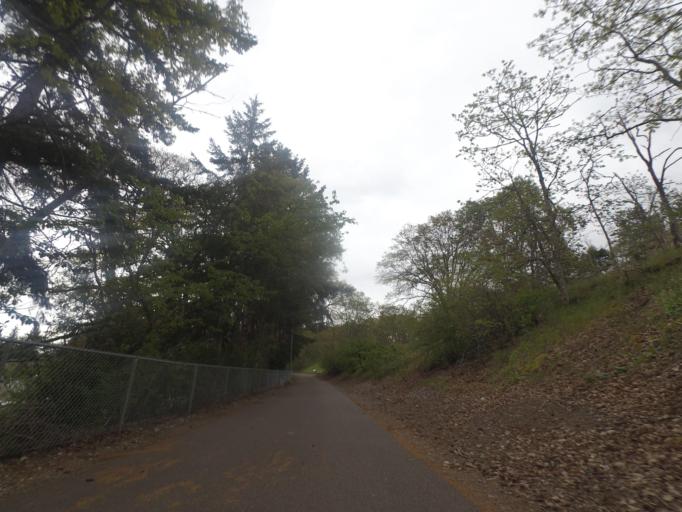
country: US
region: Washington
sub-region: Pierce County
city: Lakewood
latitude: 47.1867
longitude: -122.4787
